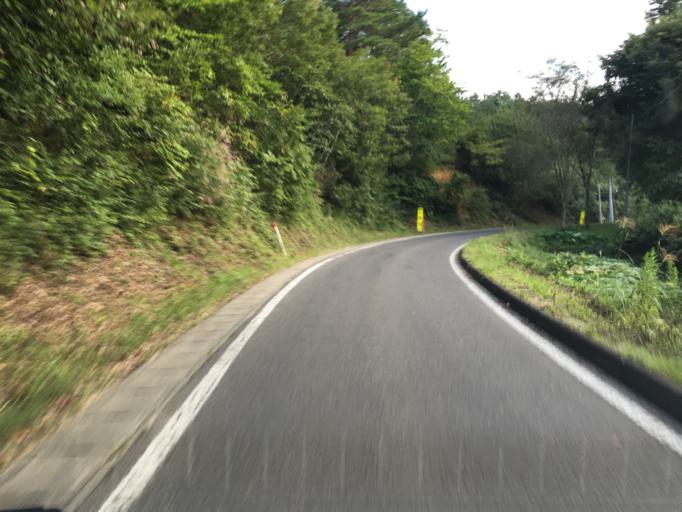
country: JP
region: Fukushima
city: Fukushima-shi
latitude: 37.6874
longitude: 140.5735
